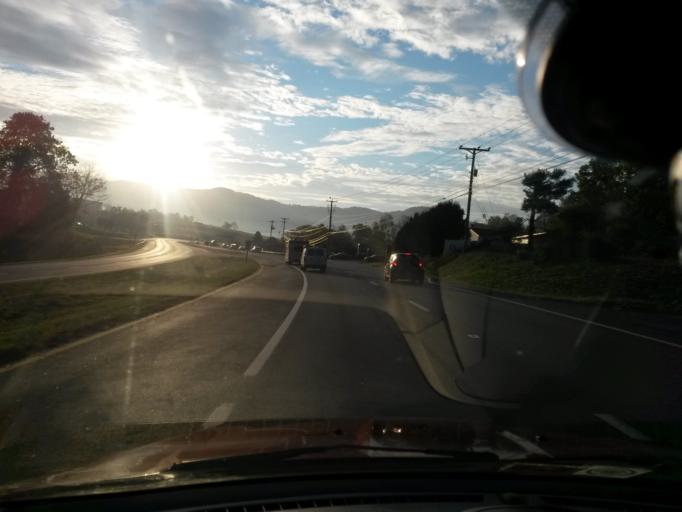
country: US
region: Virginia
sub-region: Botetourt County
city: Laymantown
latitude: 37.3437
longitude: -79.8809
